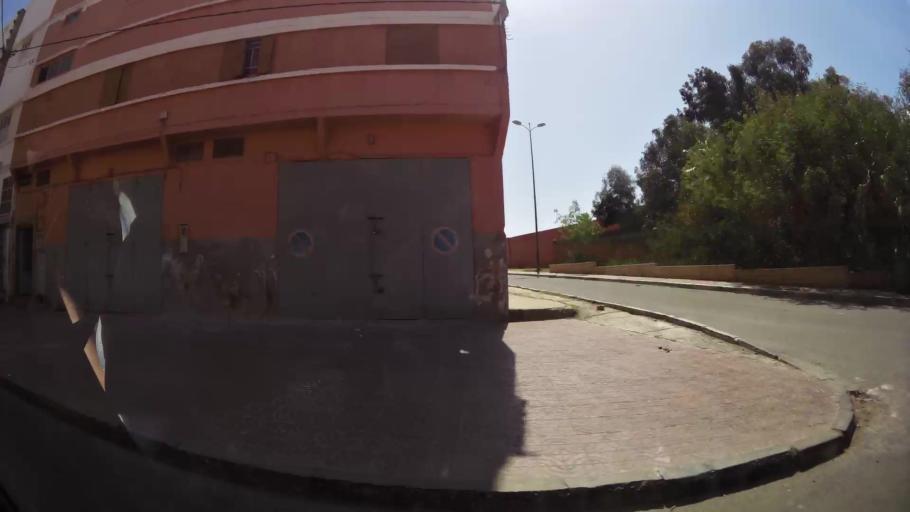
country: MA
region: Souss-Massa-Draa
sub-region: Inezgane-Ait Mellou
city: Inezgane
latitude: 30.3514
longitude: -9.5356
